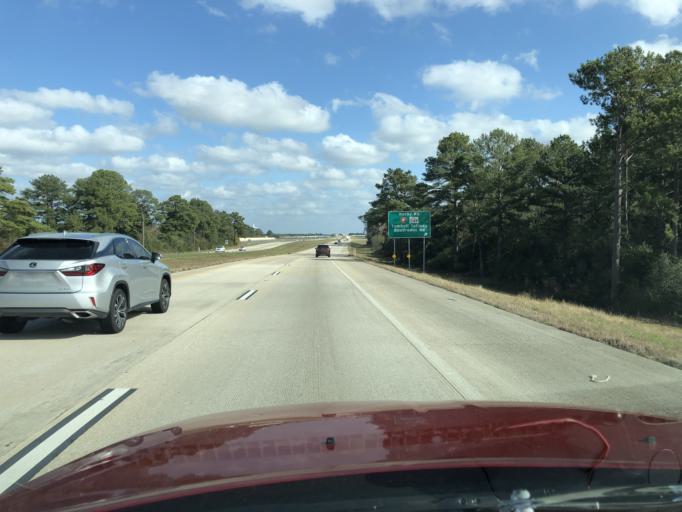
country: US
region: Texas
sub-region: Harris County
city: Tomball
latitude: 30.0522
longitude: -95.6367
